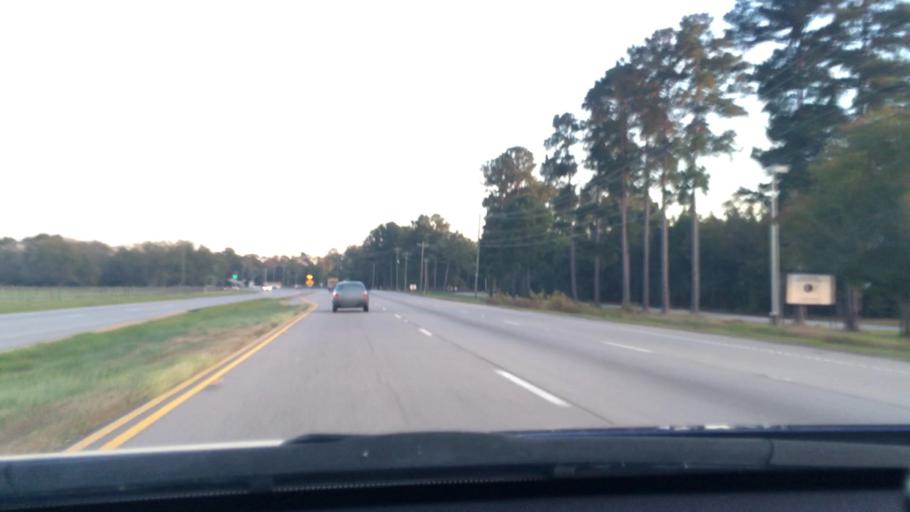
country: US
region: South Carolina
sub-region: Richland County
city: Hopkins
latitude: 33.9433
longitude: -80.8048
